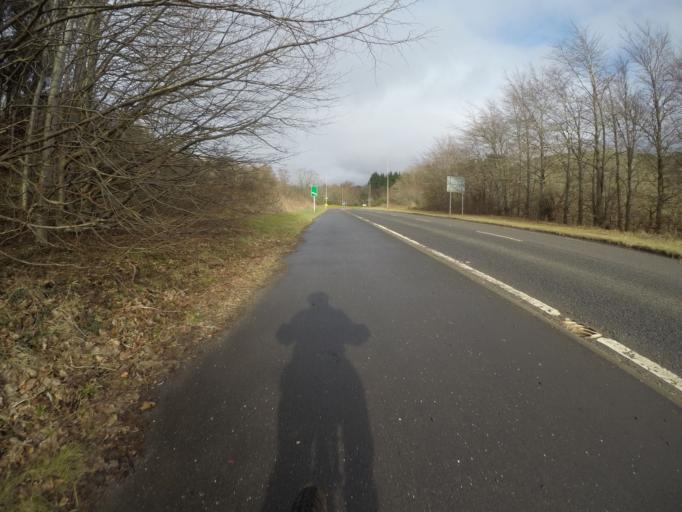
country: GB
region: Scotland
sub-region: North Ayrshire
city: Fairlie
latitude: 55.7425
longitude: -4.8592
